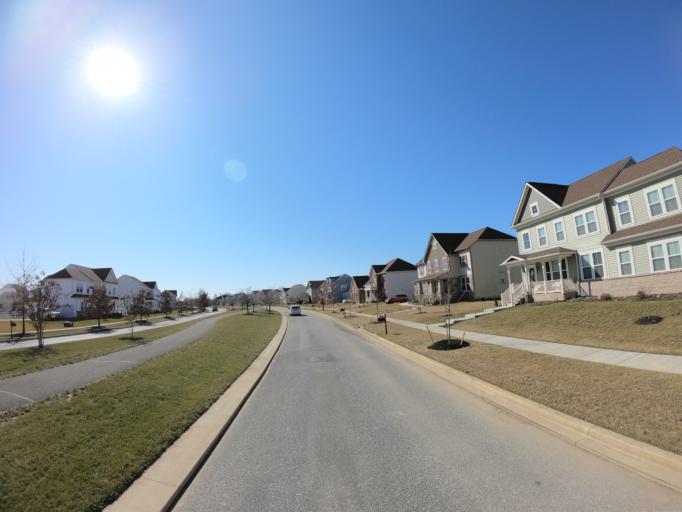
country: US
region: Delaware
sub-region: New Castle County
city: Middletown
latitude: 39.5087
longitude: -75.6664
